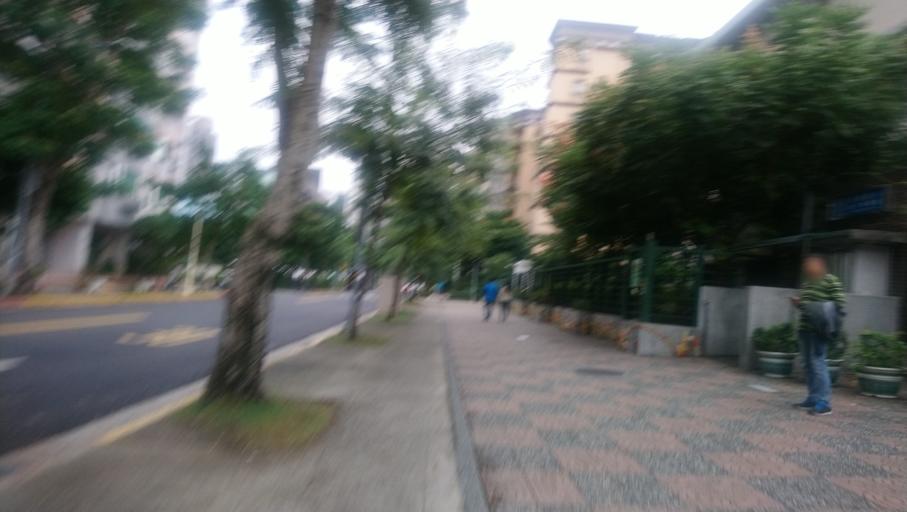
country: TW
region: Taipei
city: Taipei
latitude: 25.0320
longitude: 121.5632
